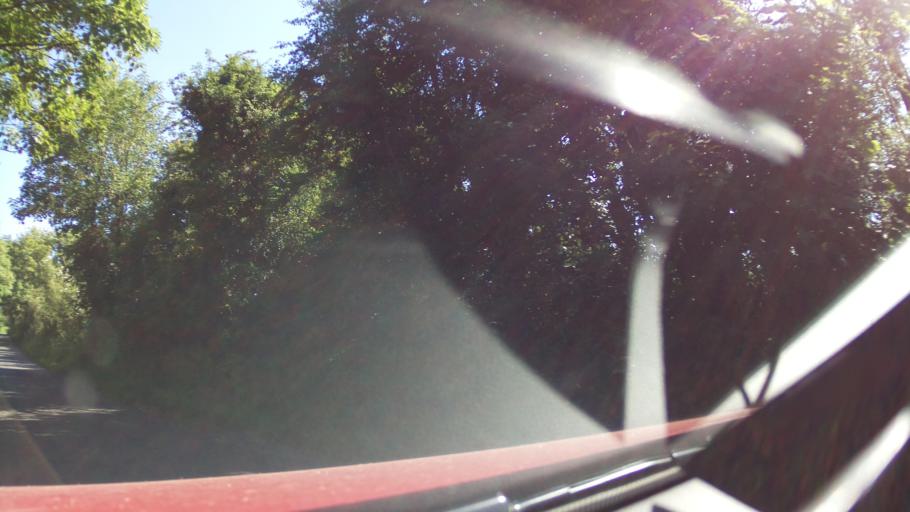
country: GB
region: England
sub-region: Hampshire
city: Winchester
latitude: 51.0813
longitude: -1.3447
